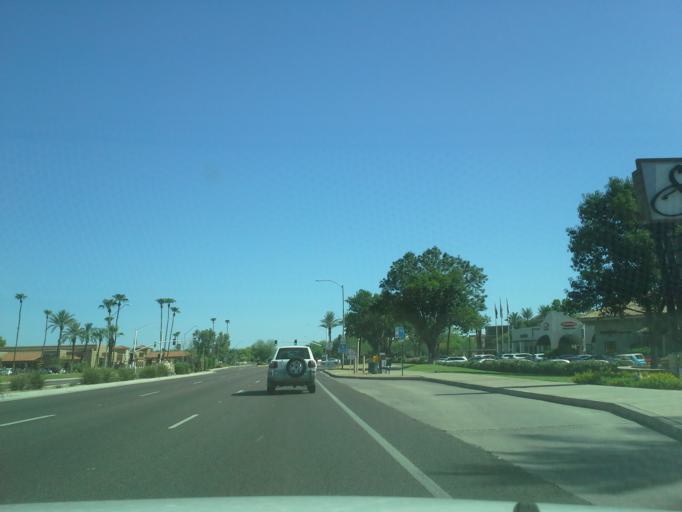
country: US
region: Arizona
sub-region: Maricopa County
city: Paradise Valley
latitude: 33.5387
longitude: -111.9256
